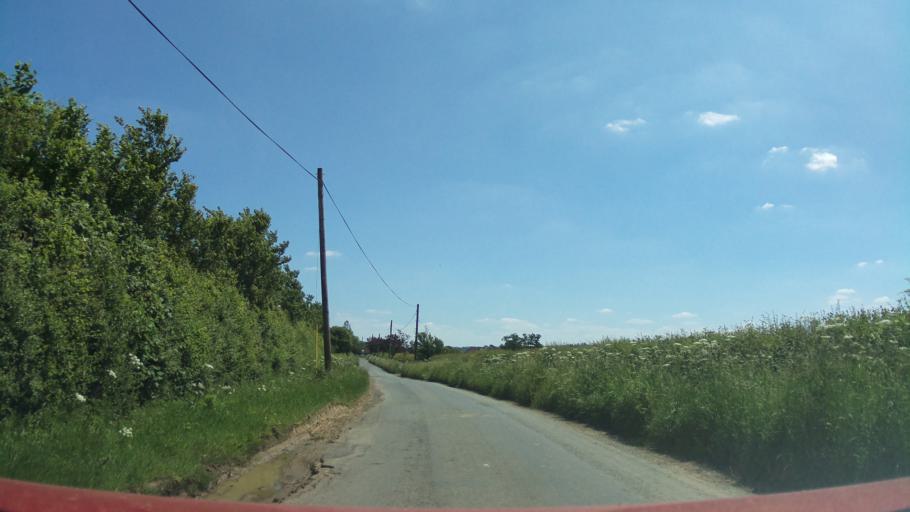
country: GB
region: England
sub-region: Wiltshire
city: Bremhill
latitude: 51.4621
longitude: -2.0685
